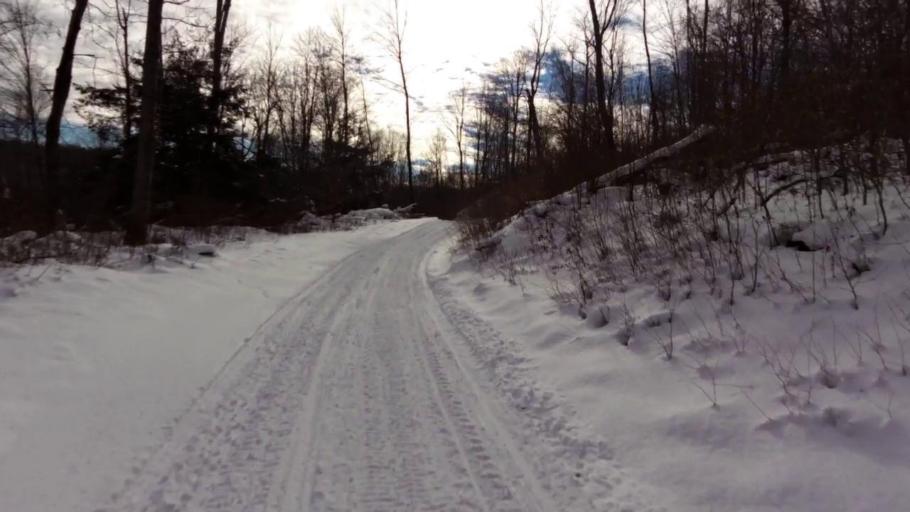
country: US
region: Pennsylvania
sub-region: McKean County
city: Foster Brook
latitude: 42.0121
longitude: -78.5367
